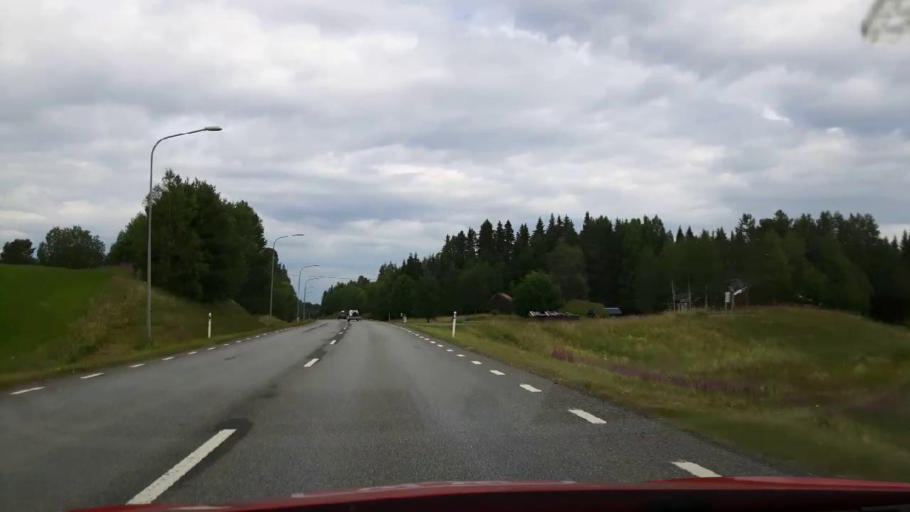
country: SE
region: Jaemtland
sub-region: Stroemsunds Kommun
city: Stroemsund
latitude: 63.6654
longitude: 15.3908
